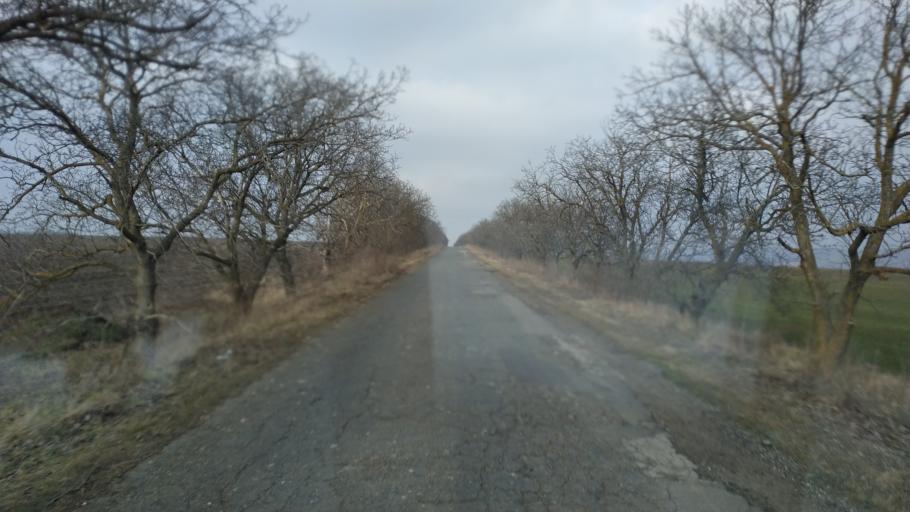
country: MD
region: Hincesti
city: Dancu
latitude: 46.8857
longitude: 28.3002
